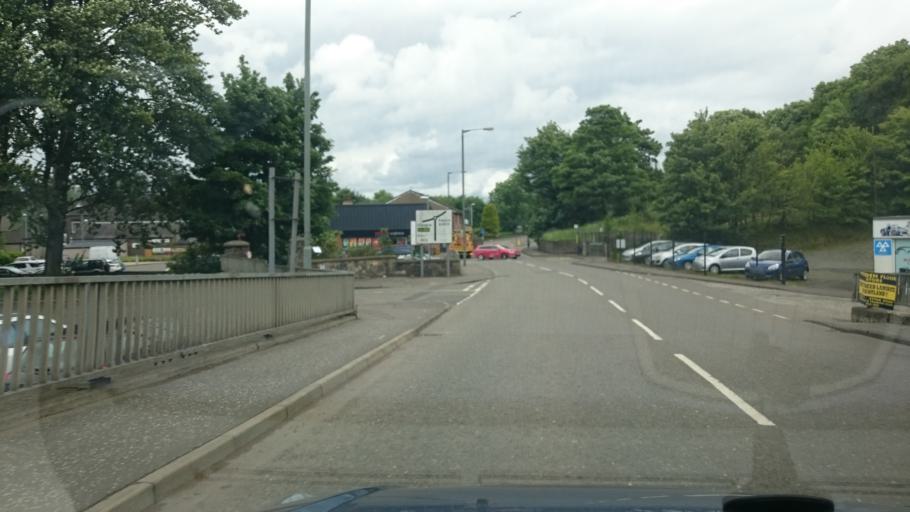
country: GB
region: Scotland
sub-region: Falkirk
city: Bonnybridge
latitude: 56.0001
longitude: -3.8877
